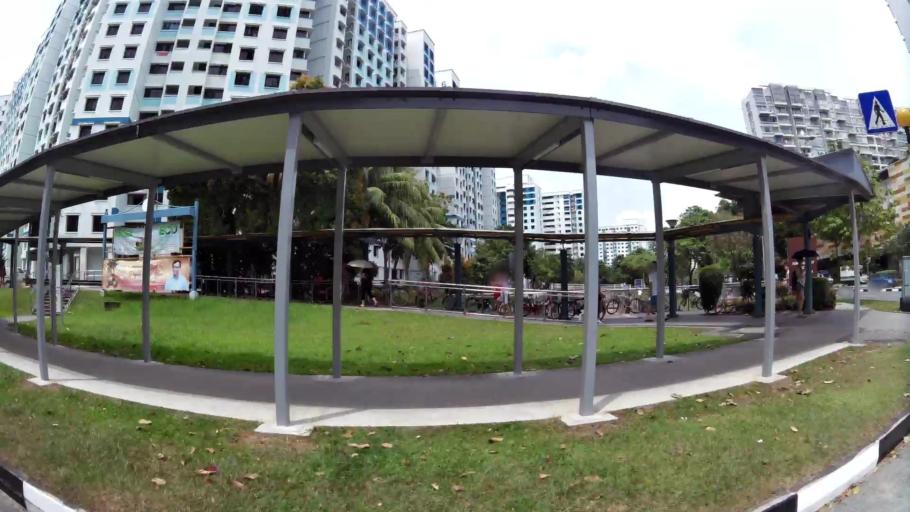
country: MY
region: Johor
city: Johor Bahru
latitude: 1.3384
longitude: 103.7042
